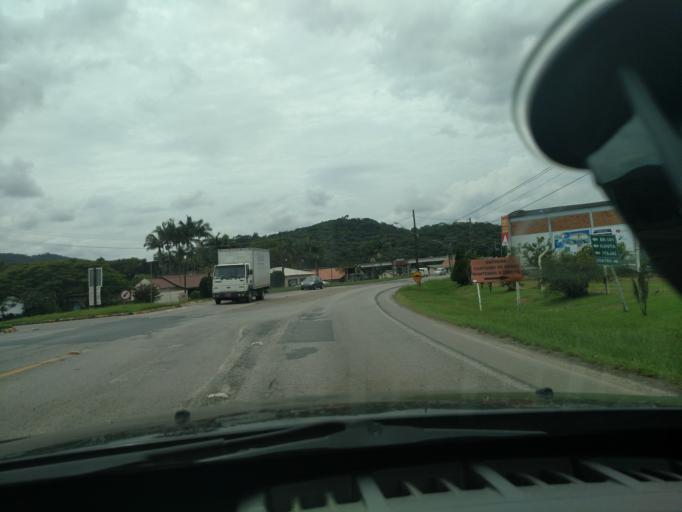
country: BR
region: Santa Catarina
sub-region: Gaspar
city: Gaspar
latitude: -26.9108
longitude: -48.9349
